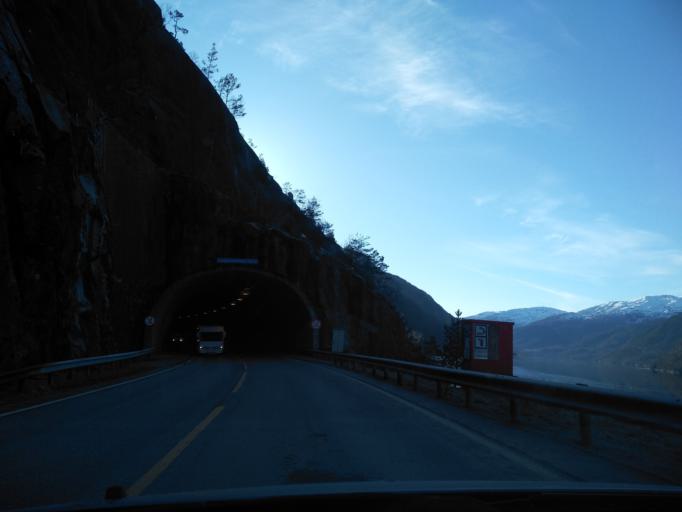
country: NO
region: Rogaland
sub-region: Sauda
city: Sauda
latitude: 59.8455
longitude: 6.3348
